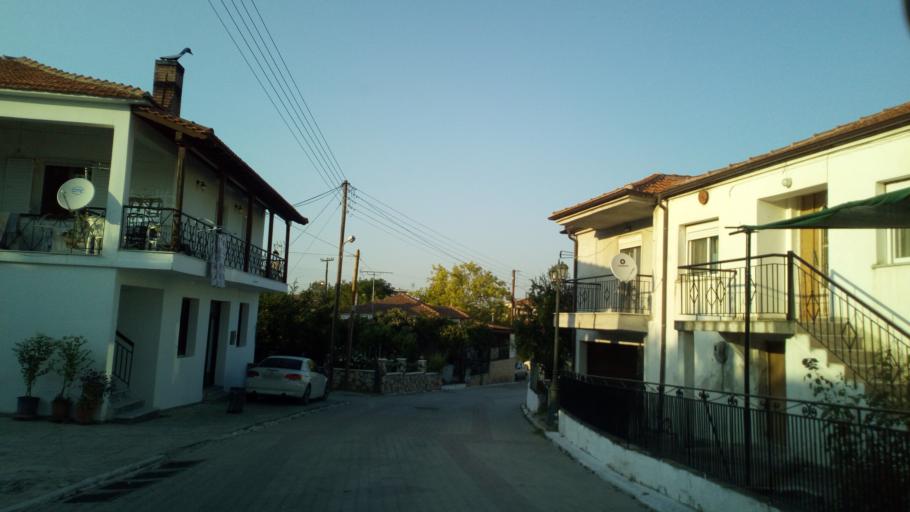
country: GR
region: Central Macedonia
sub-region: Nomos Chalkidikis
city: Pefkochori
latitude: 39.9422
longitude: 23.6632
